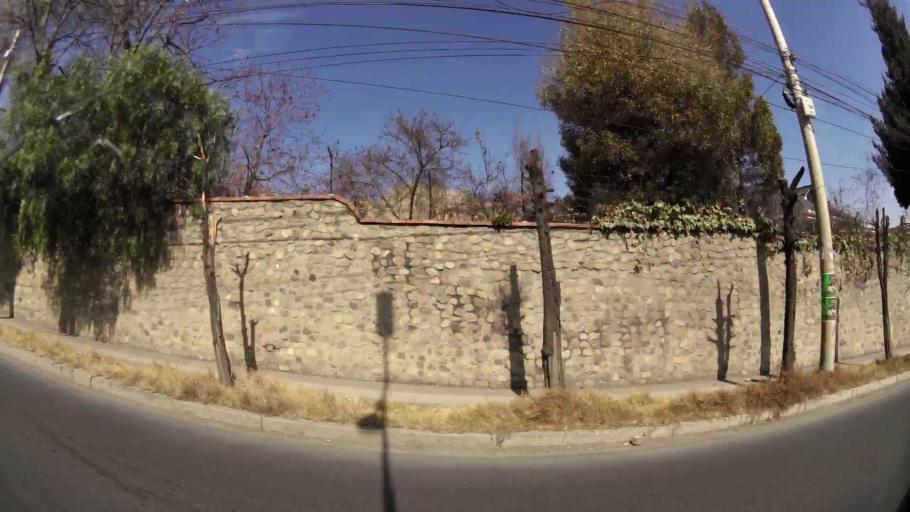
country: BO
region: La Paz
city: La Paz
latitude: -16.5267
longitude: -68.0685
